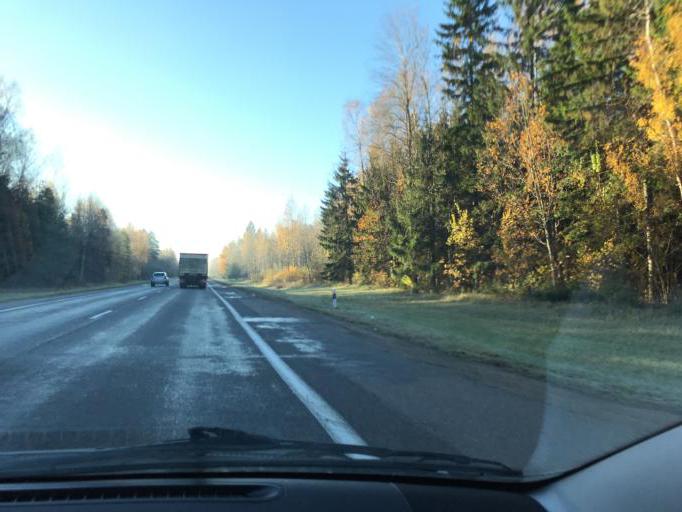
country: BY
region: Vitebsk
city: Vitebsk
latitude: 54.9490
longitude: 30.3614
